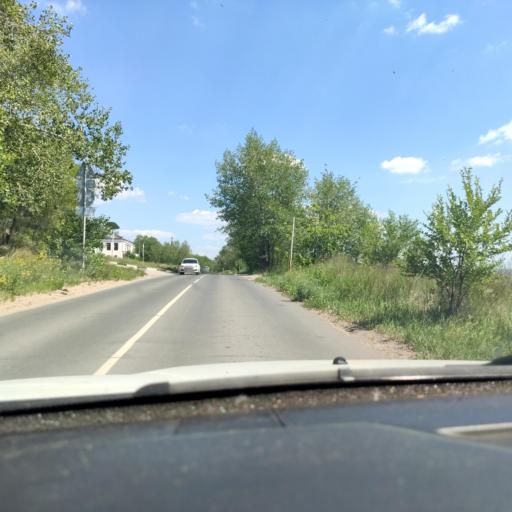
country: RU
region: Samara
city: Pribrezhnyy
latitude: 53.4834
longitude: 49.8444
